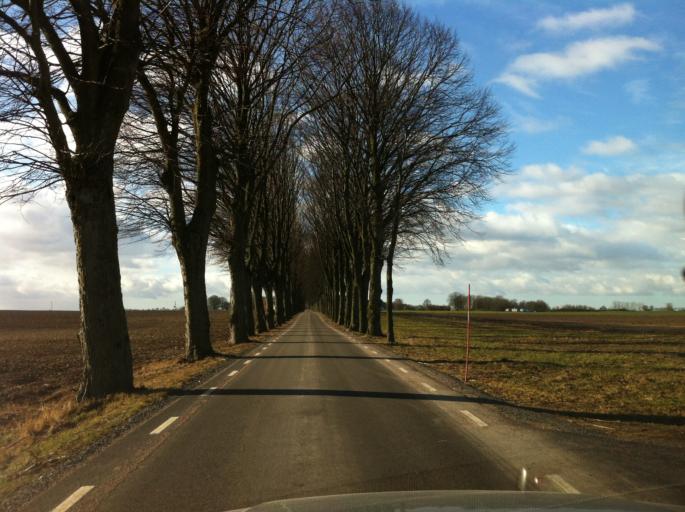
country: SE
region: Skane
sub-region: Landskrona
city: Asmundtorp
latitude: 55.9445
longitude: 13.0101
